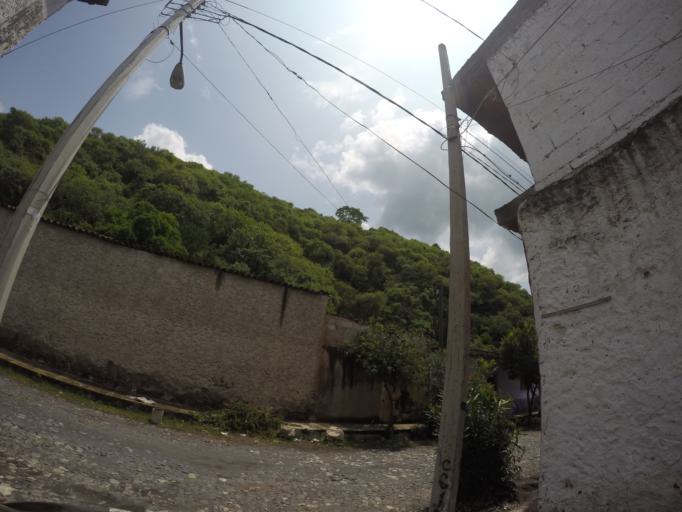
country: MX
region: Nayarit
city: Jala
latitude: 21.1062
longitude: -104.4380
